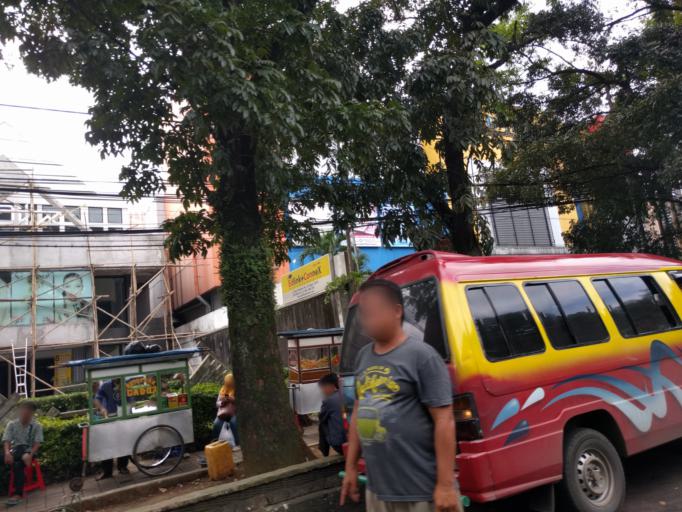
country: ID
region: West Java
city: Bogor
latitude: -6.6064
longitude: 106.8087
